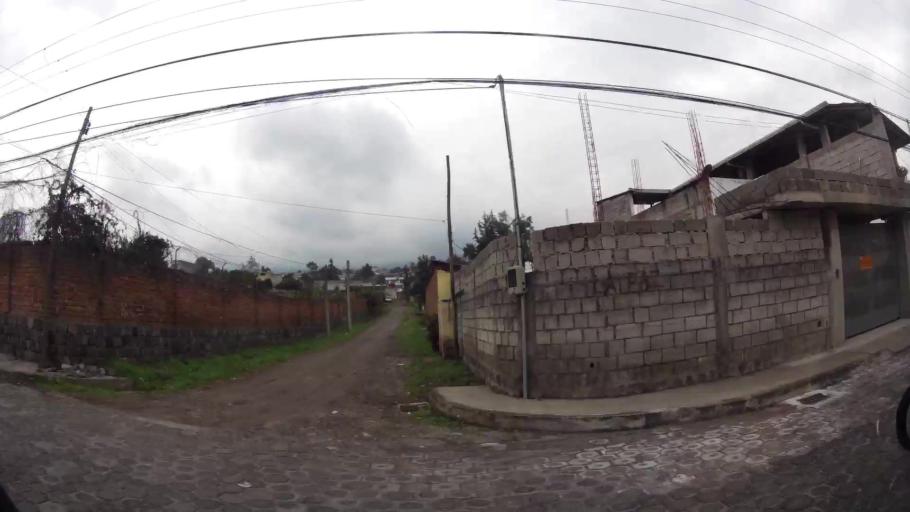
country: EC
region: Pichincha
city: Sangolqui
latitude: -0.2958
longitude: -78.4692
